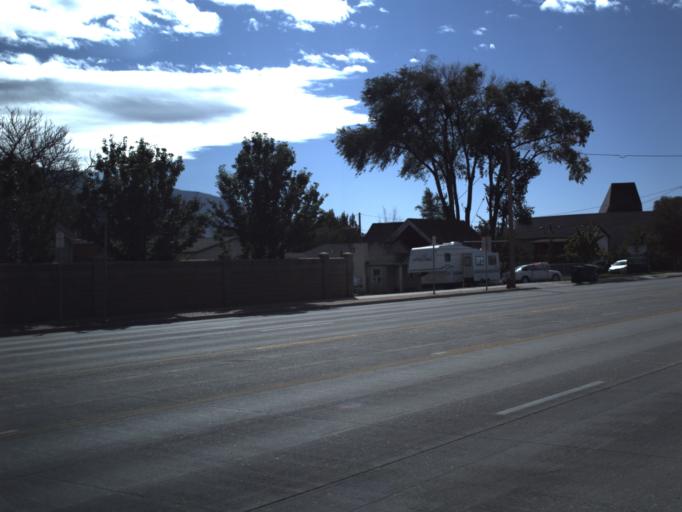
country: US
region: Utah
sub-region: Salt Lake County
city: West Jordan
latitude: 40.6183
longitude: -111.9389
